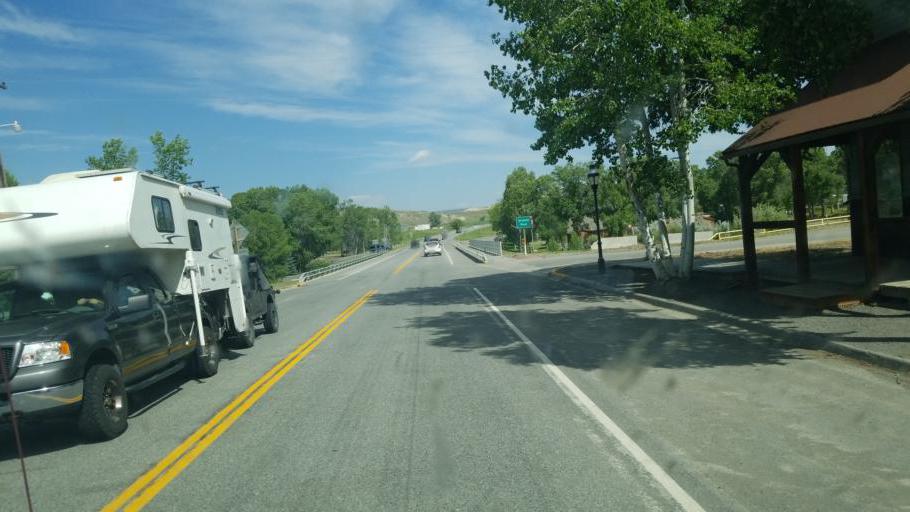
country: US
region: Wyoming
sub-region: Park County
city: Cody
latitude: 44.1582
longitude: -108.8721
